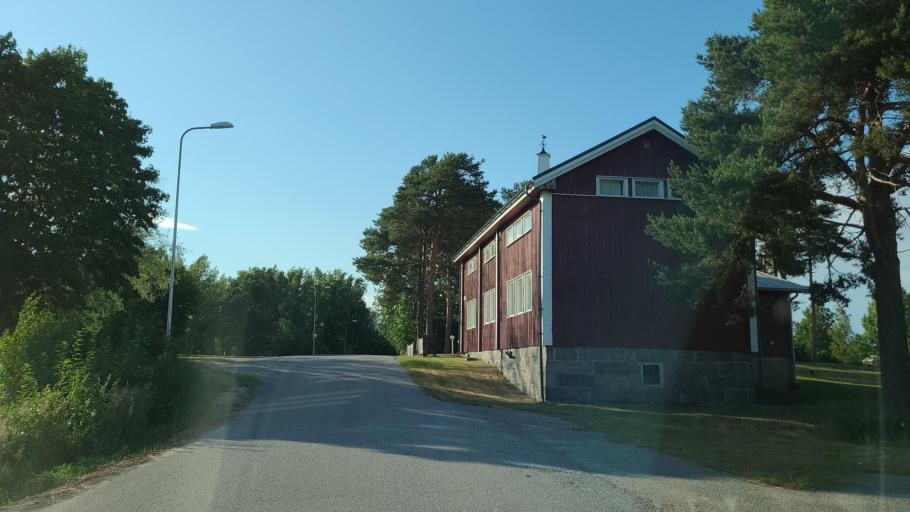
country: FI
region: Ostrobothnia
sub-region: Vaasa
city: Replot
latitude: 63.3463
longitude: 21.3337
